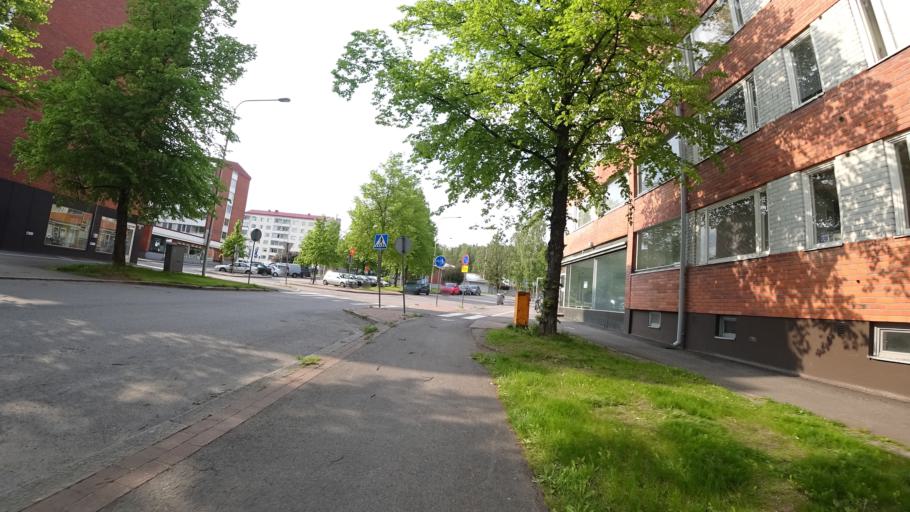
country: FI
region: Pirkanmaa
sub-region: Tampere
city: Pirkkala
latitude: 61.4975
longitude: 23.6399
